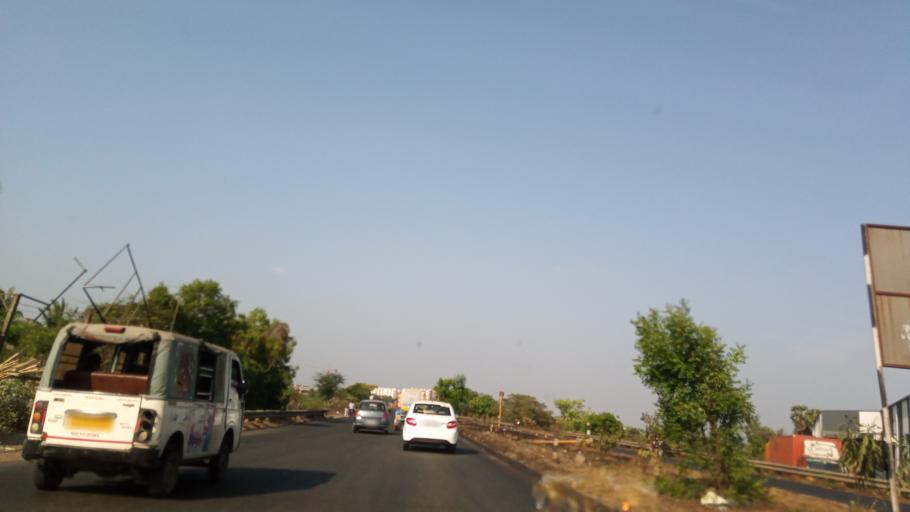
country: IN
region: Tamil Nadu
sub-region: Kancheepuram
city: Nandambakkam
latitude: 13.0184
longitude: 80.0107
